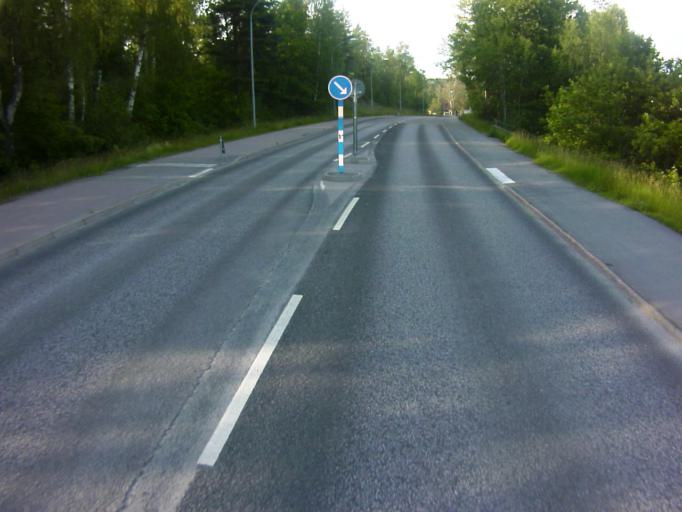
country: SE
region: Soedermanland
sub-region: Eskilstuna Kommun
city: Skogstorp
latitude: 59.3232
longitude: 16.4796
